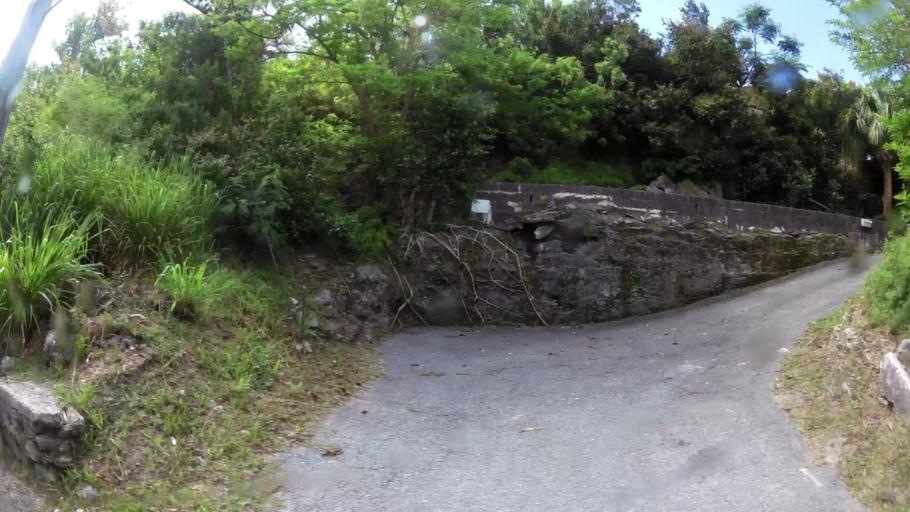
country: BM
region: Saint George
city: Saint George
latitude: 32.3684
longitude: -64.6523
